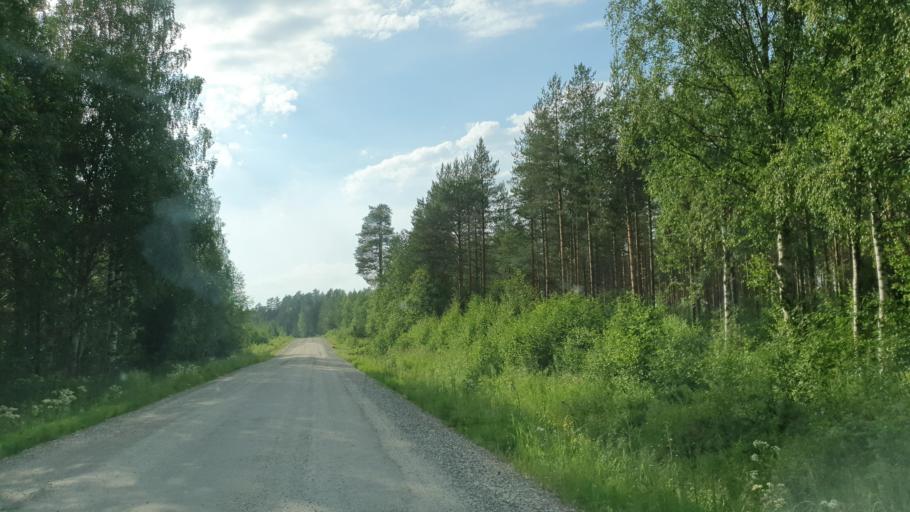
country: FI
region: Kainuu
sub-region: Kehys-Kainuu
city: Kuhmo
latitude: 64.0956
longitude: 29.6270
